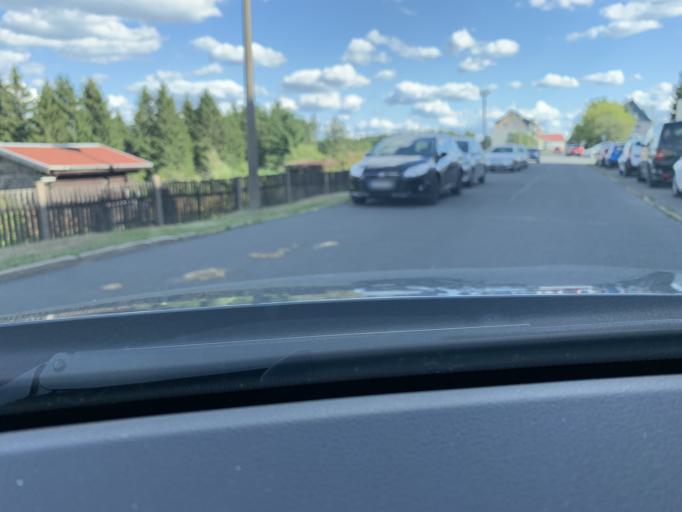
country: DE
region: Thuringia
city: Neuhaus am Rennweg
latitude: 50.5067
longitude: 11.1472
